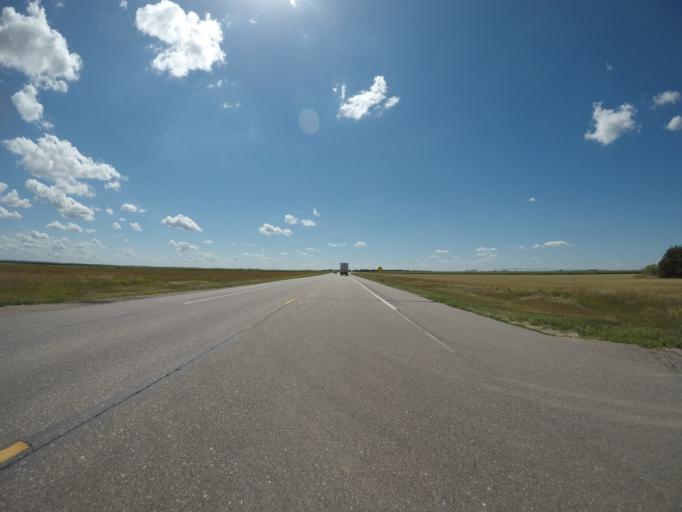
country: US
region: Nebraska
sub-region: Chase County
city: Imperial
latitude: 40.4943
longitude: -101.5904
